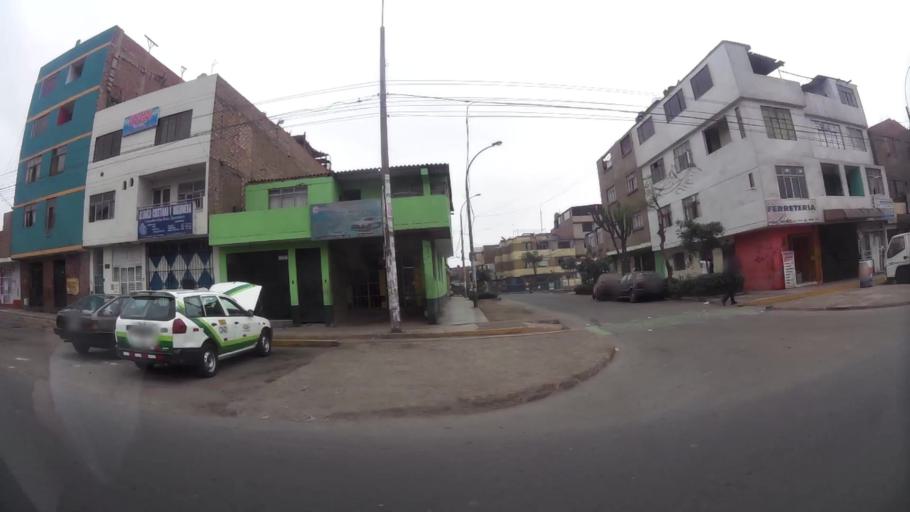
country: PE
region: Lima
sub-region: Lima
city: Independencia
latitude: -12.0206
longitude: -77.0756
